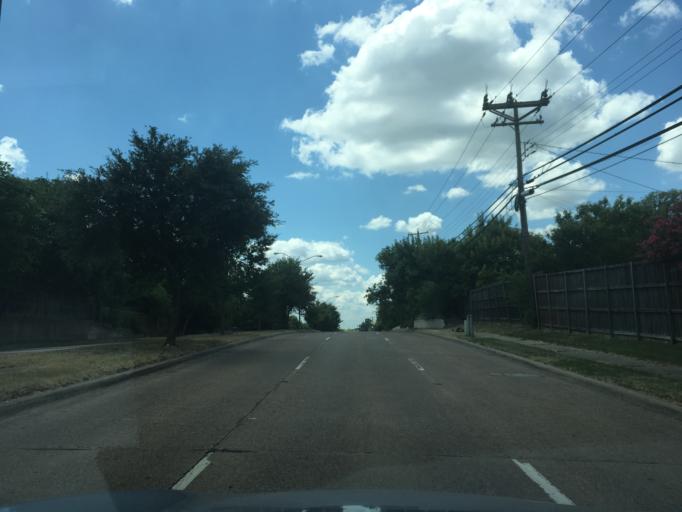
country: US
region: Texas
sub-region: Dallas County
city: Richardson
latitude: 32.8753
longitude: -96.7180
